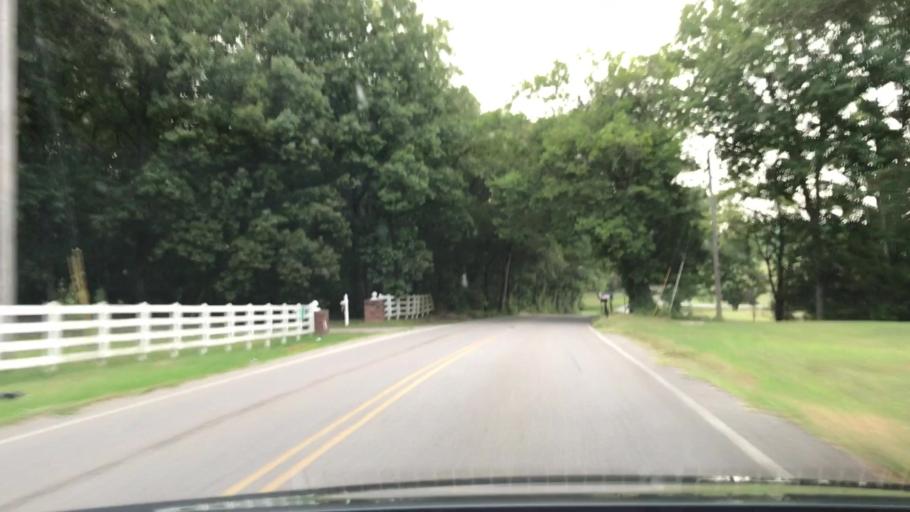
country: US
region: Tennessee
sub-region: Williamson County
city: Nolensville
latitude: 35.9767
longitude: -86.6613
